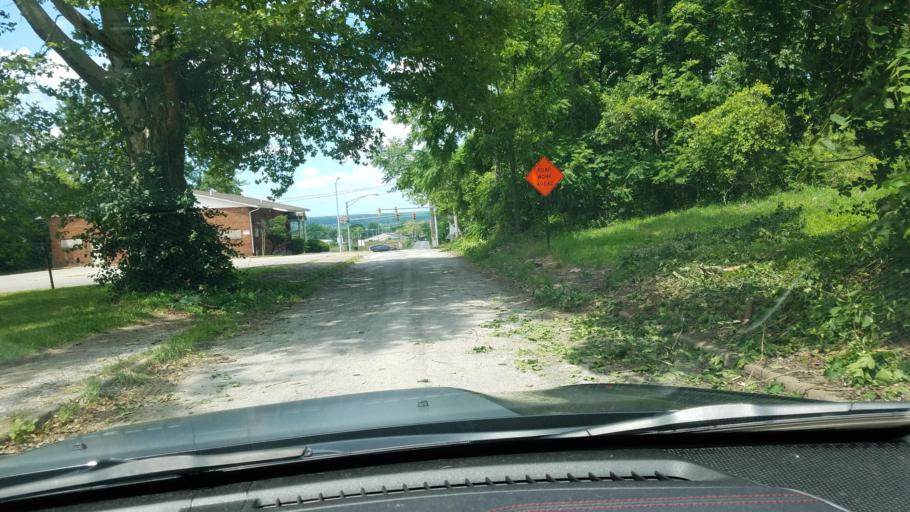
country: US
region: Ohio
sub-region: Mahoning County
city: Youngstown
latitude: 41.0953
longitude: -80.6319
